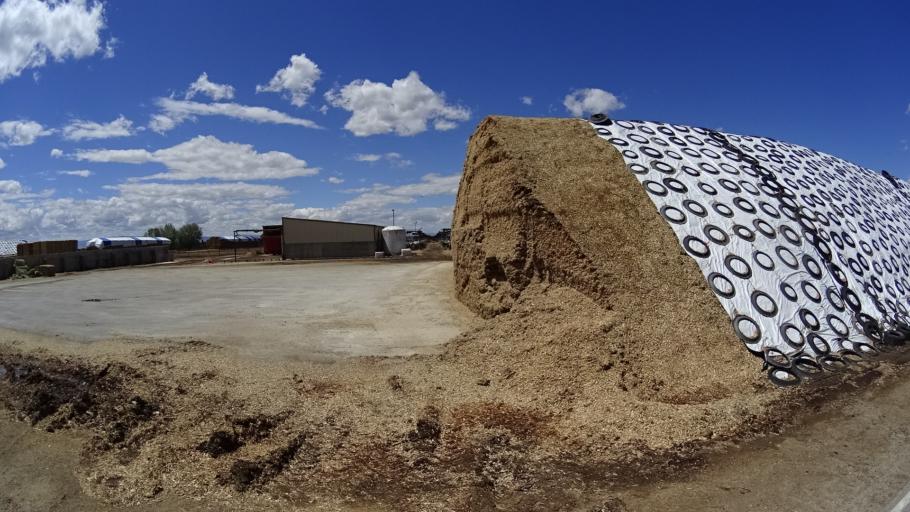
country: US
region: Idaho
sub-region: Ada County
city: Kuna
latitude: 43.5514
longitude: -116.4537
